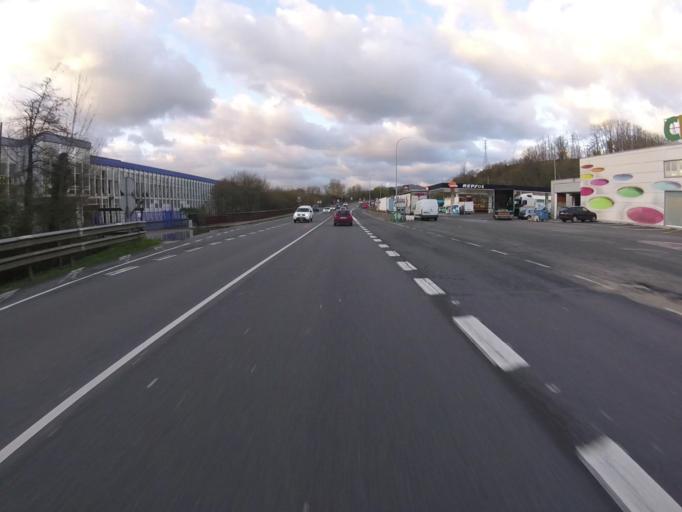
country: ES
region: Basque Country
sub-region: Provincia de Guipuzcoa
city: Lezo
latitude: 43.3125
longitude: -1.8784
